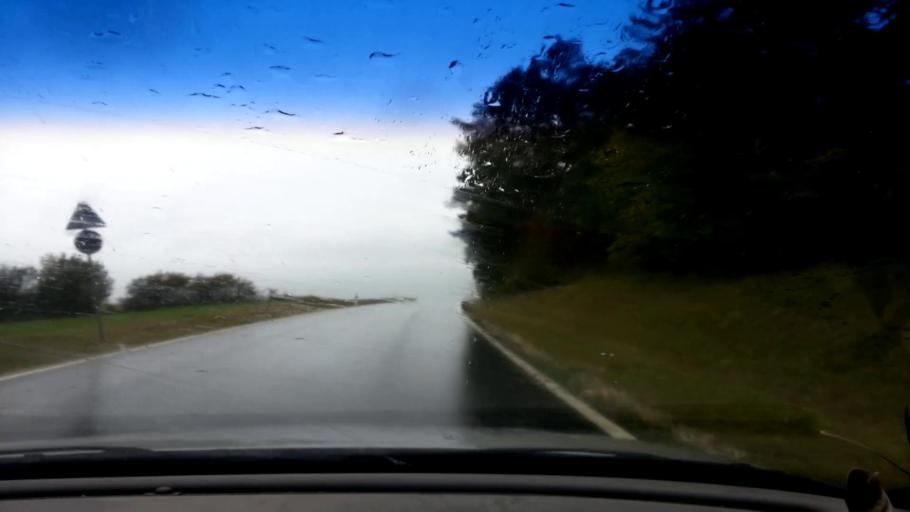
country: DE
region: Bavaria
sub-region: Upper Franconia
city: Heiligenstadt
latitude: 49.8999
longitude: 11.1540
